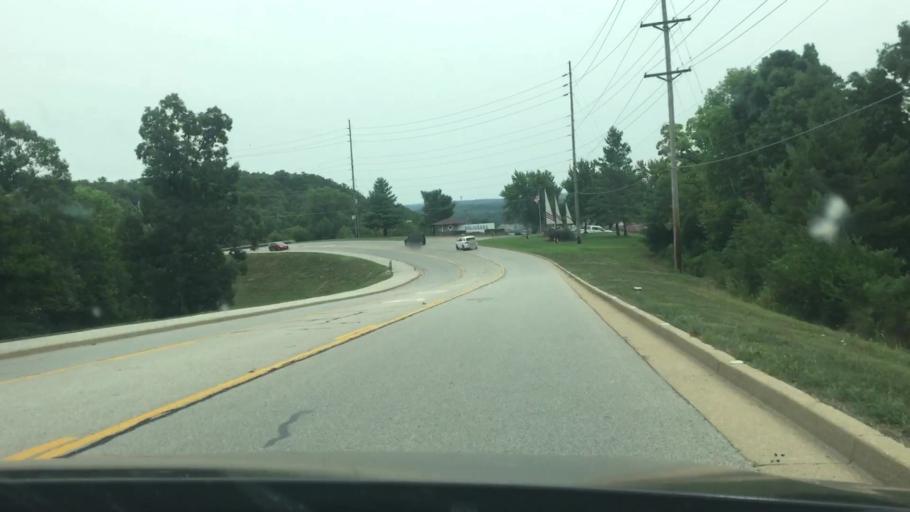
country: US
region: Missouri
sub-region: Miller County
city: Lake Ozark
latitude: 38.1922
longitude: -92.6711
